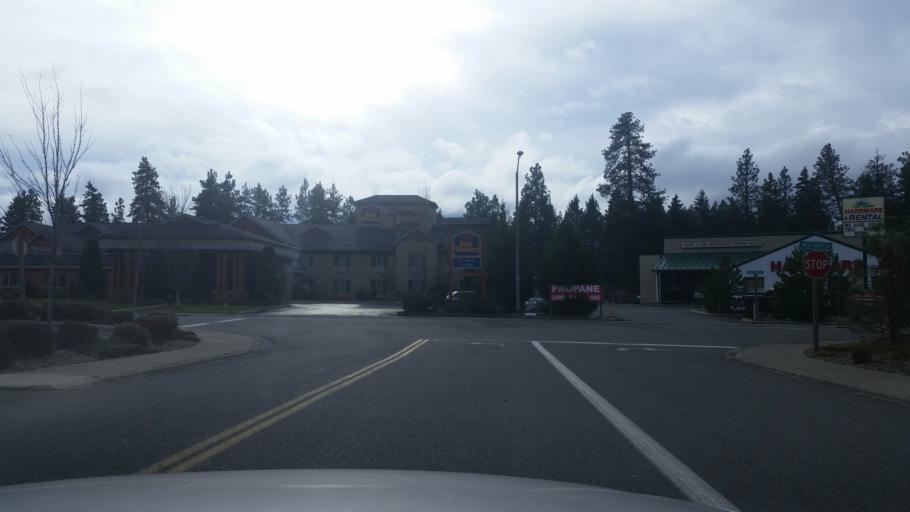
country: US
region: Washington
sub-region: Kittitas County
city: Cle Elum
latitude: 47.1952
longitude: -120.9552
